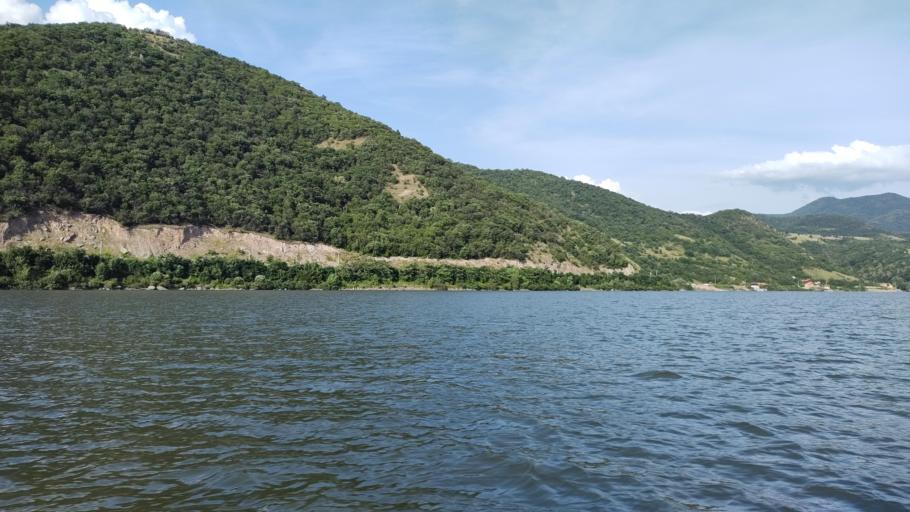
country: RO
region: Mehedinti
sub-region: Comuna Svinita
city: Svinita
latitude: 44.5431
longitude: 22.0470
